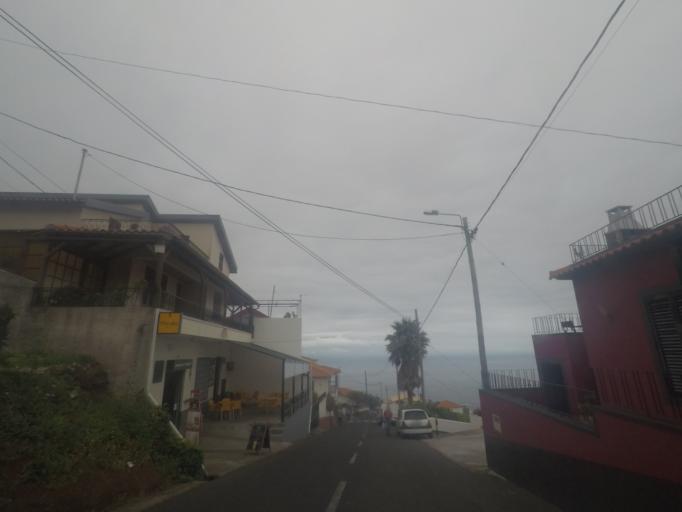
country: PT
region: Madeira
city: Camara de Lobos
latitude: 32.6678
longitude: -16.9682
